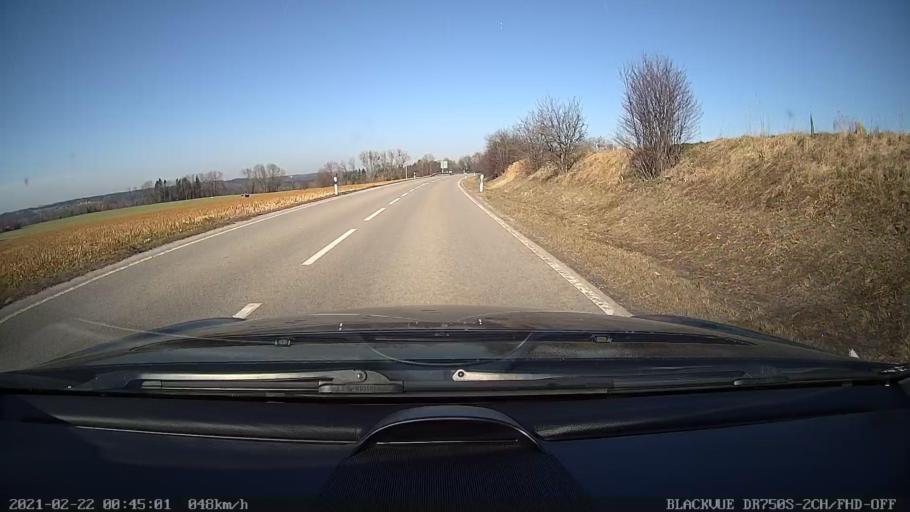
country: DE
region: Bavaria
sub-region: Upper Bavaria
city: Griesstatt
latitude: 47.9900
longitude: 12.1740
